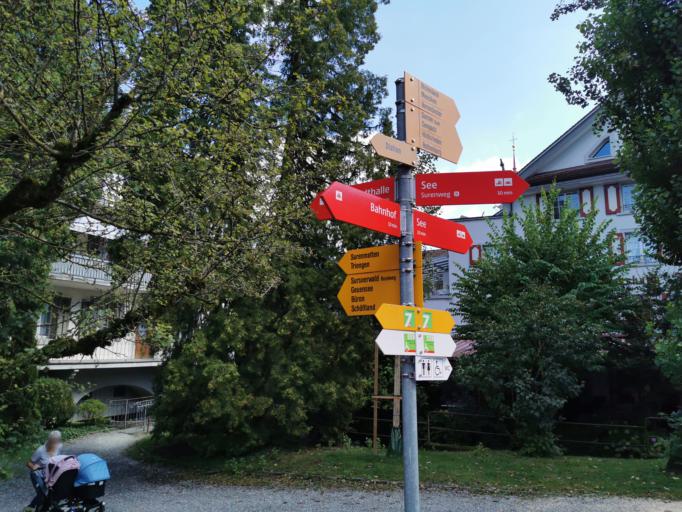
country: CH
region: Lucerne
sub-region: Sursee District
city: Sursee
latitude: 47.1726
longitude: 8.1077
